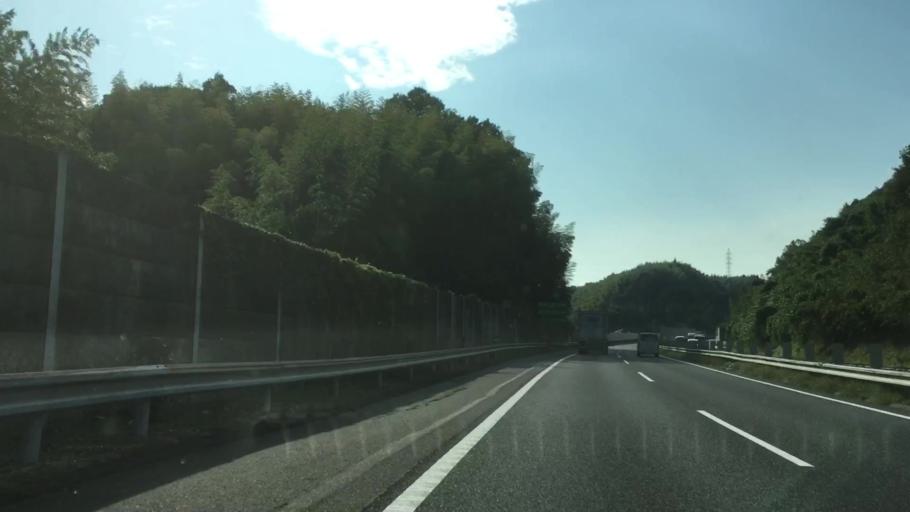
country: JP
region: Yamaguchi
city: Hikari
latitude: 34.0272
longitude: 131.9572
